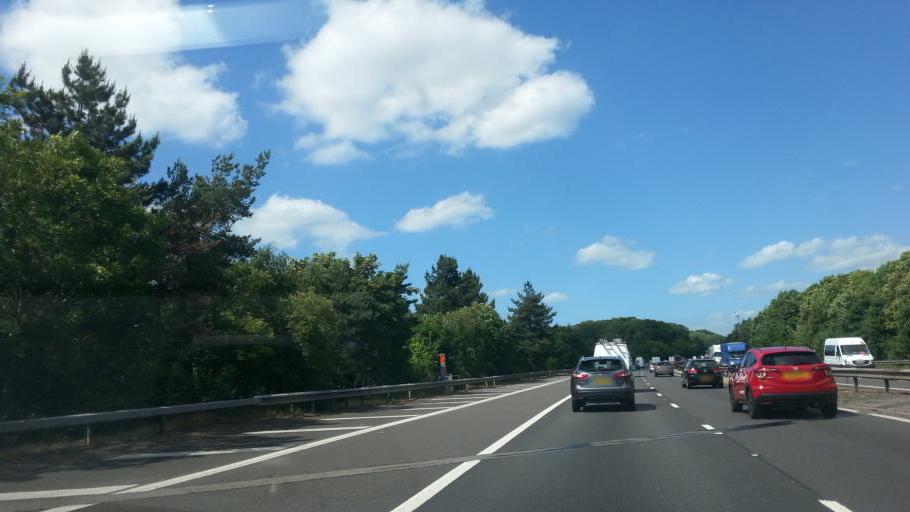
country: GB
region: England
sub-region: Hertfordshire
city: Welwyn
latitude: 51.8336
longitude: -0.2082
